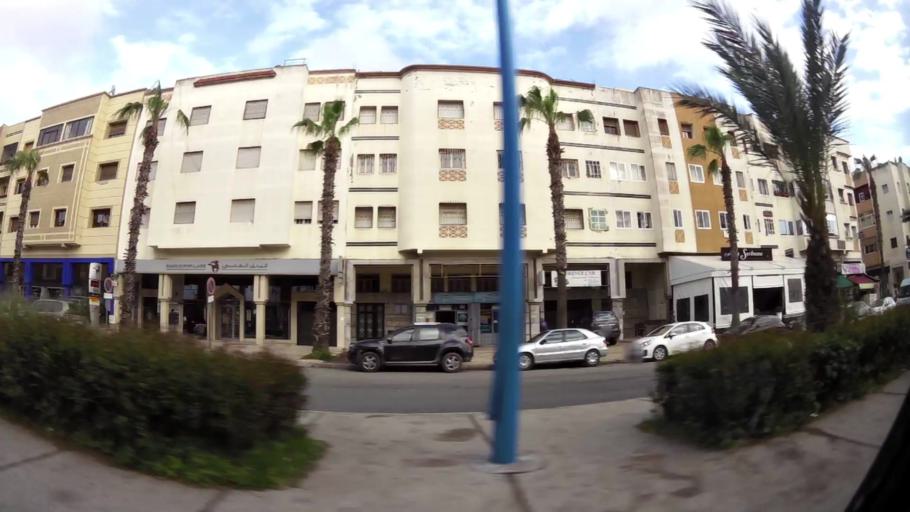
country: MA
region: Grand Casablanca
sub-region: Mohammedia
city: Mohammedia
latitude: 33.6892
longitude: -7.3775
